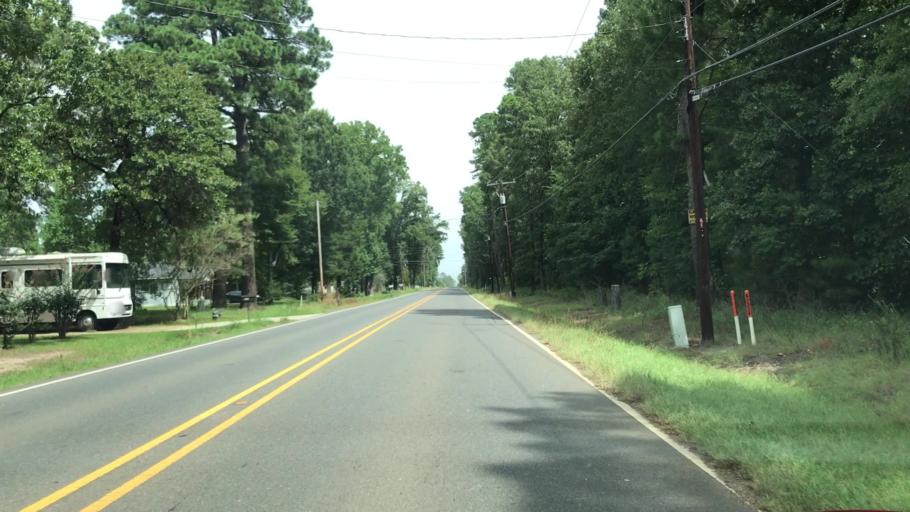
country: US
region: Louisiana
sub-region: De Soto Parish
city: Stonewall
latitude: 32.3804
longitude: -93.7634
